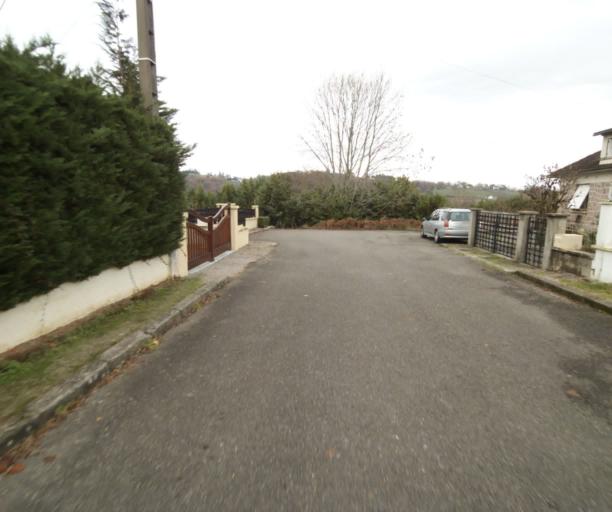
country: FR
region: Limousin
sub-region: Departement de la Correze
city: Tulle
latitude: 45.2698
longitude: 1.7370
